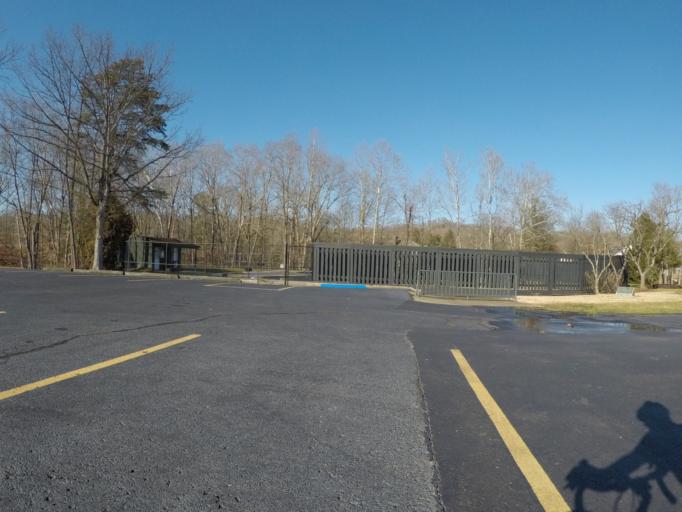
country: US
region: West Virginia
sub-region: Cabell County
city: Pea Ridge
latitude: 38.4189
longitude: -82.3279
